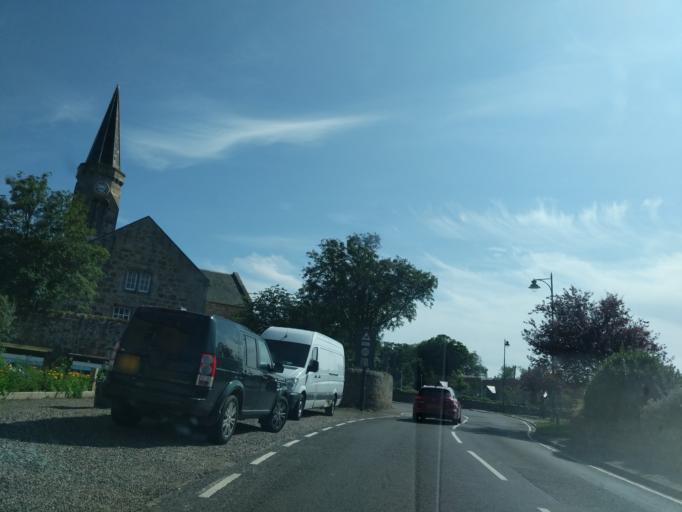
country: GB
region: Scotland
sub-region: Fife
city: Anstruther
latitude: 56.2998
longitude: -2.6597
